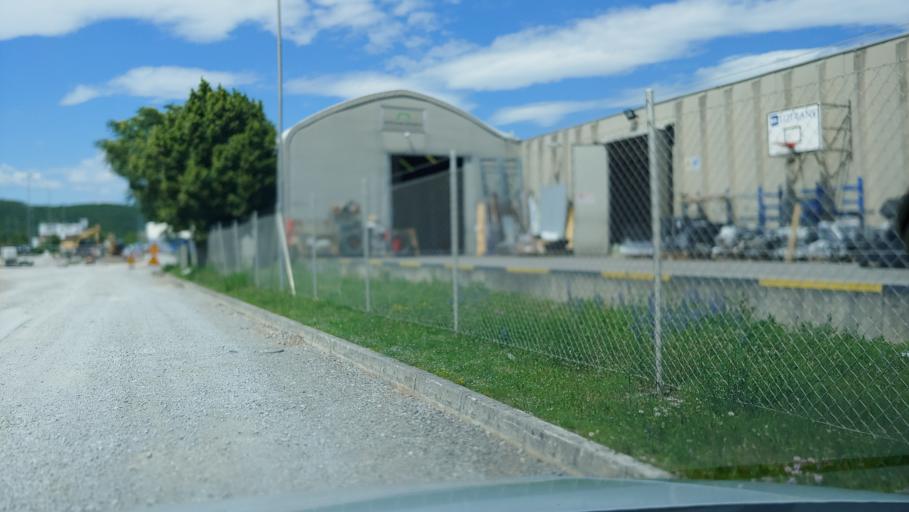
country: SI
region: Sezana
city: Sezana
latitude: 45.6992
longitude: 13.8480
